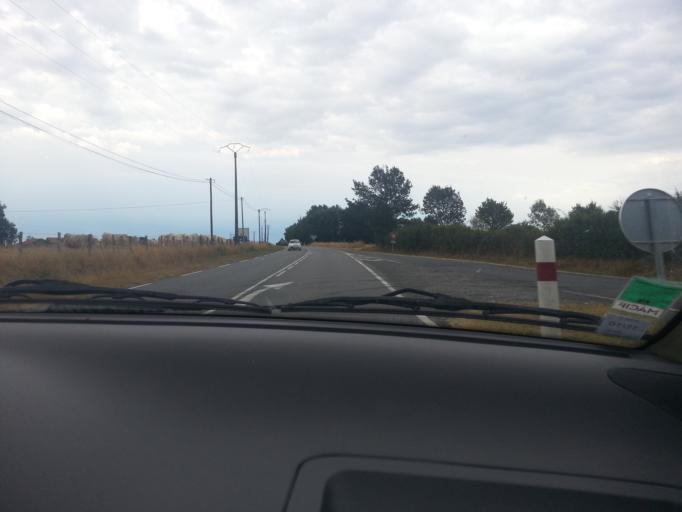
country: FR
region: Auvergne
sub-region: Departement de l'Allier
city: Saint-Gerand-le-Puy
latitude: 46.2097
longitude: 3.5126
